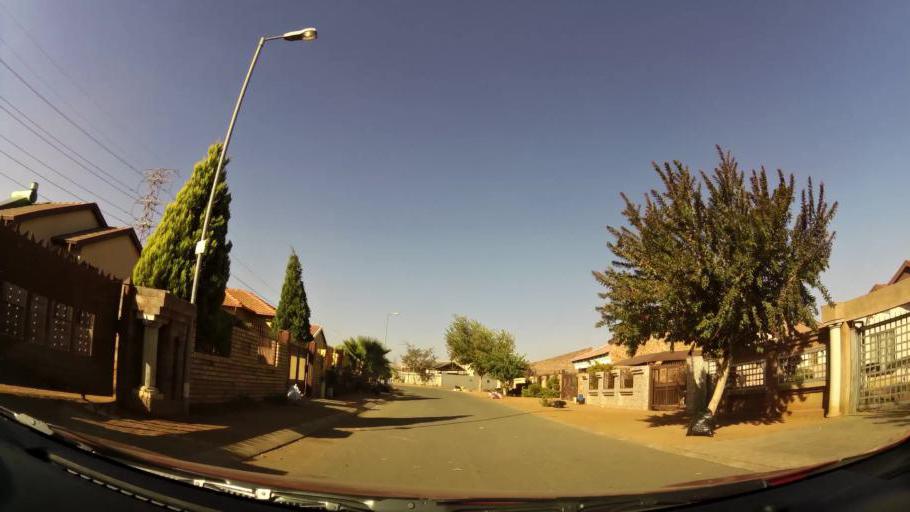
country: ZA
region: Gauteng
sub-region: City of Tshwane Metropolitan Municipality
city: Mabopane
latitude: -25.5772
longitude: 28.0907
